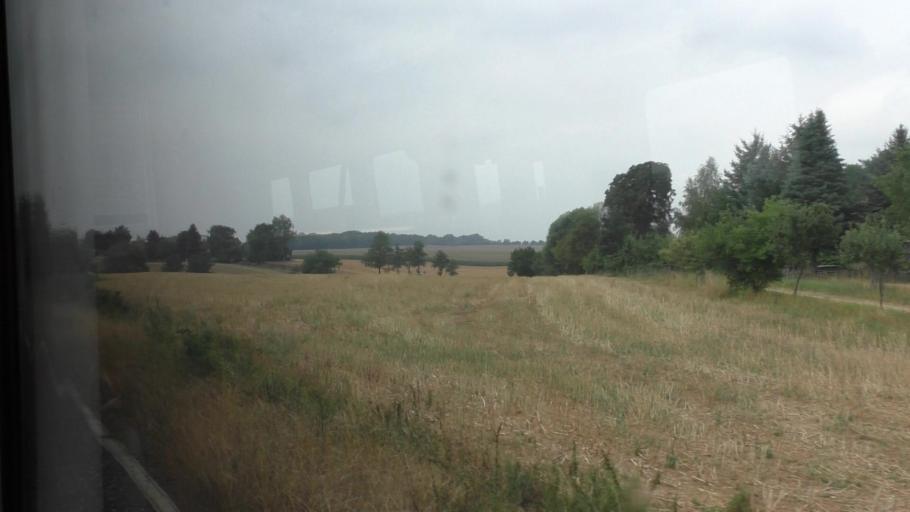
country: DE
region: Saxony
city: Hirschfelde
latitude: 50.9167
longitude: 14.8516
